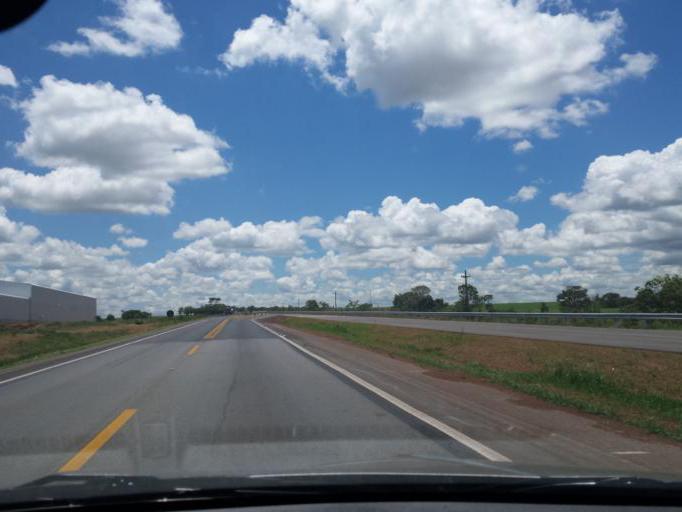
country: BR
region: Goias
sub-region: Cristalina
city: Cristalina
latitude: -16.6638
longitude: -47.7200
